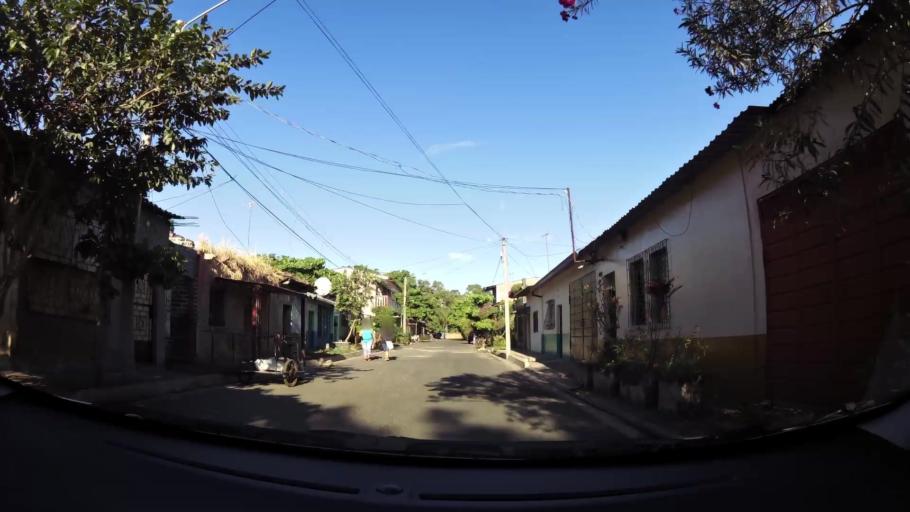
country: SV
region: Sonsonate
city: Sonsonate
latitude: 13.7124
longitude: -89.7203
